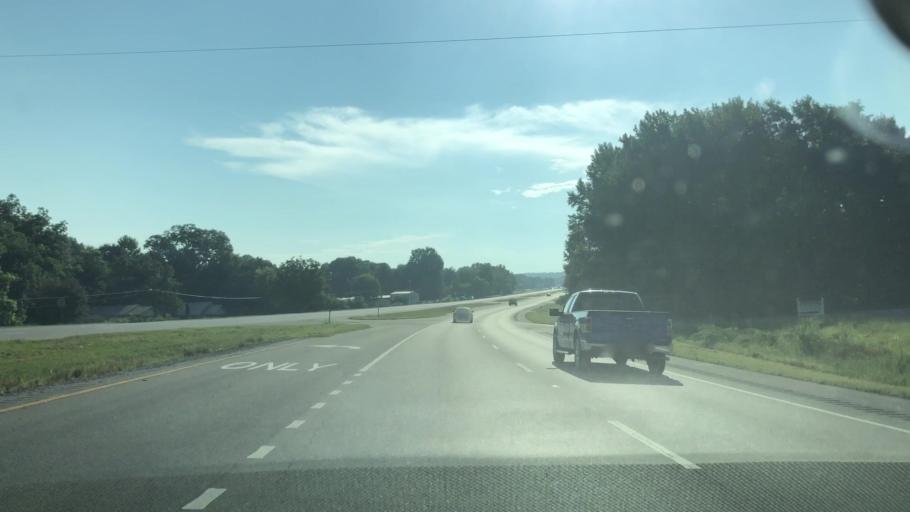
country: US
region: Alabama
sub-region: Calhoun County
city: West End-Cobb Town
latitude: 33.6471
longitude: -85.8737
